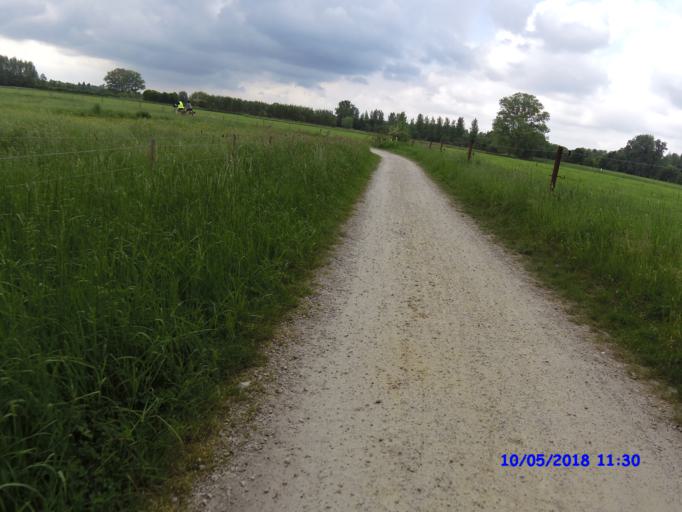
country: BE
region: Flanders
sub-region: Provincie Oost-Vlaanderen
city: Merelbeke
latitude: 51.0011
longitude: 3.7286
